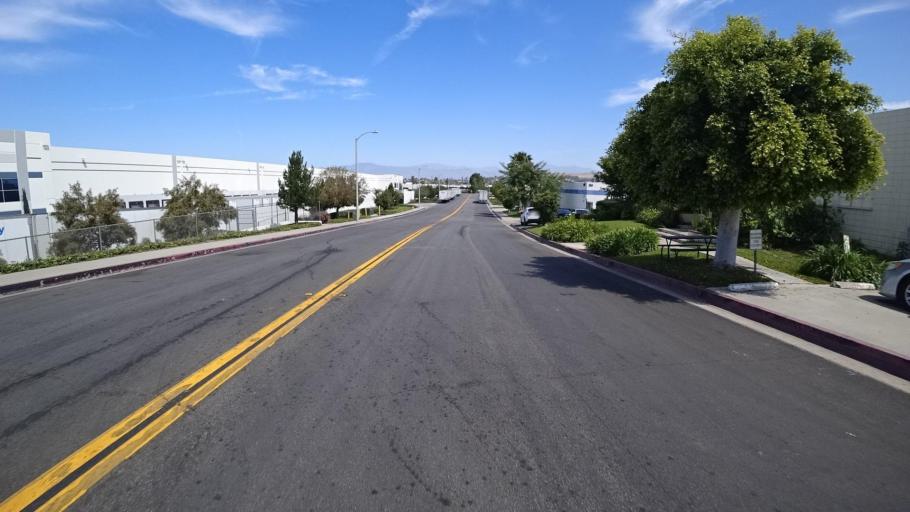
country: US
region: California
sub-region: Los Angeles County
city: South San Jose Hills
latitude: 34.0022
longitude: -117.9137
